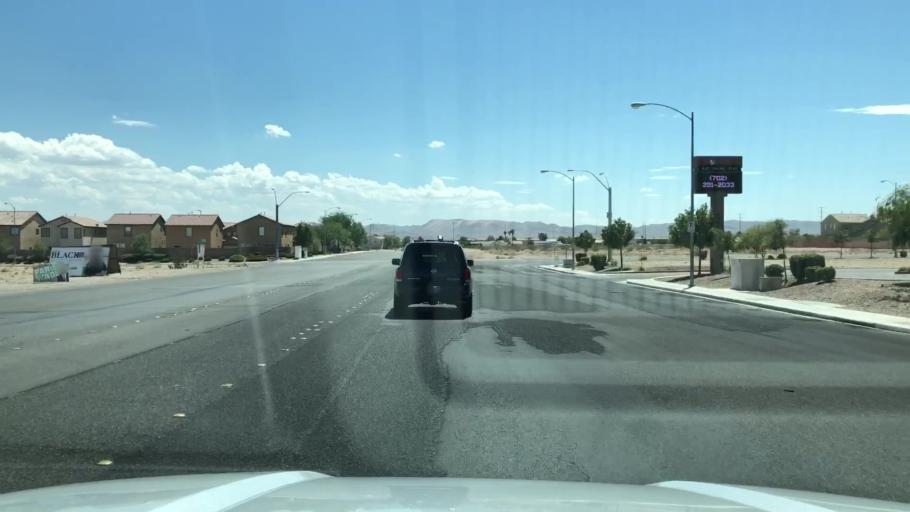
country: US
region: Nevada
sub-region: Clark County
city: Enterprise
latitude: 36.0431
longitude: -115.2081
